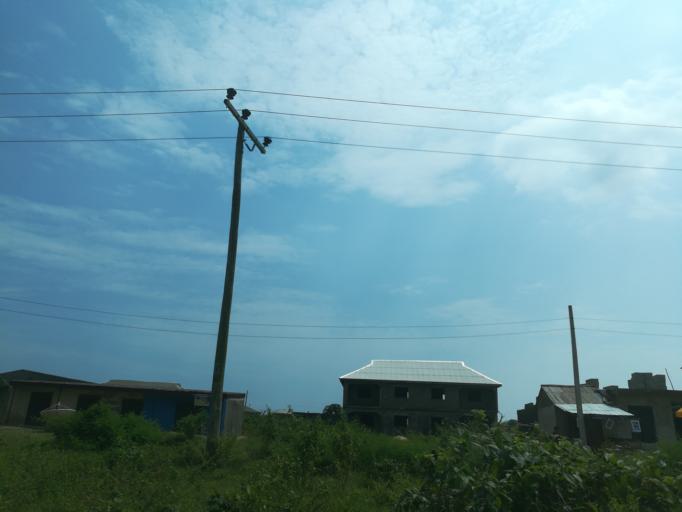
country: NG
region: Lagos
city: Ikorodu
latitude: 6.5953
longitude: 3.6346
